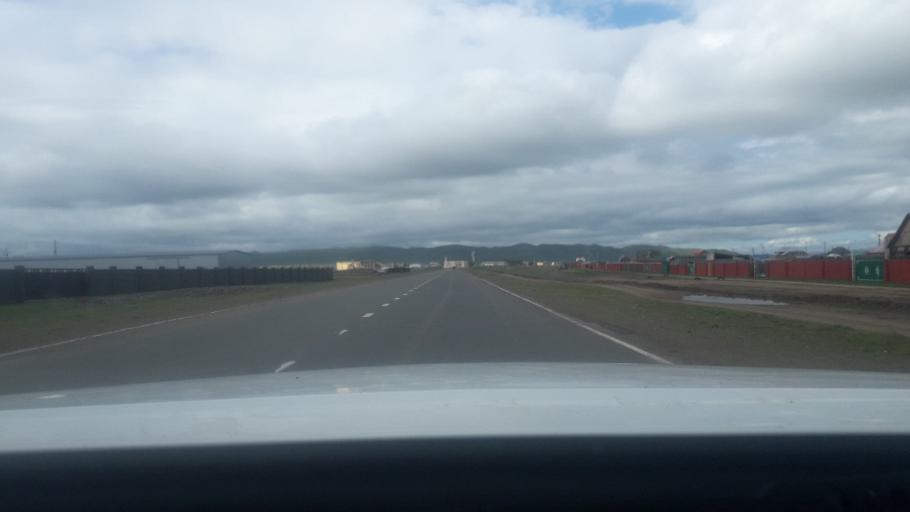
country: MN
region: Central Aimak
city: Altanbulag
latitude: 47.7585
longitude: 106.5785
